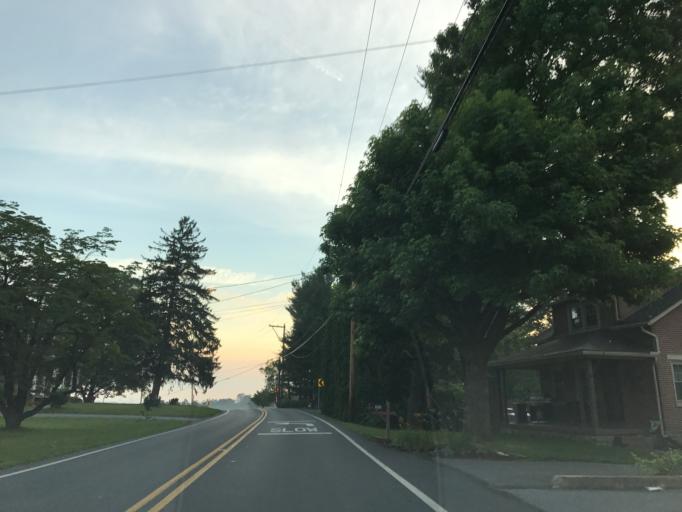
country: US
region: Pennsylvania
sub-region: Lancaster County
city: Willow Street
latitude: 39.9877
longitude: -76.3142
